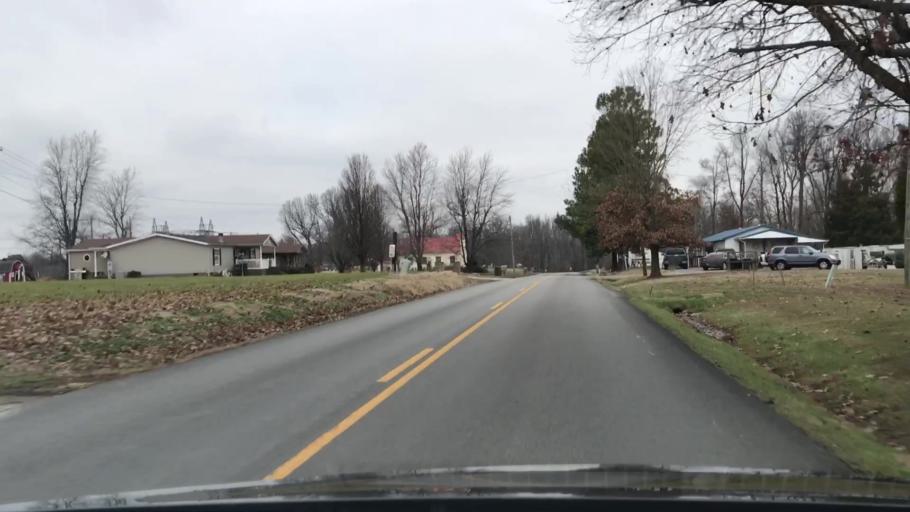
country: US
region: Kentucky
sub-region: Muhlenberg County
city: Morehead
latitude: 37.3418
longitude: -87.2216
